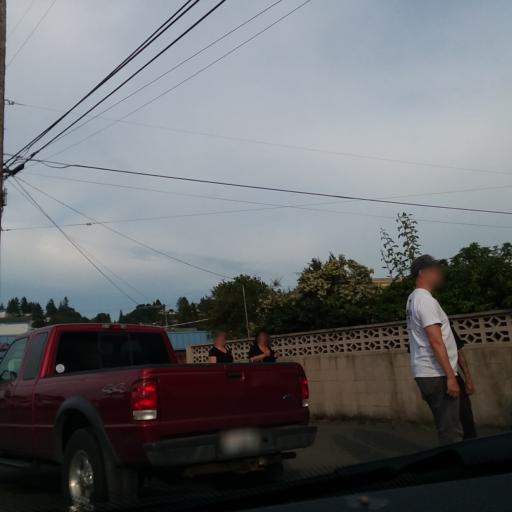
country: US
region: Washington
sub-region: King County
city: Seattle
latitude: 47.5793
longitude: -122.4098
